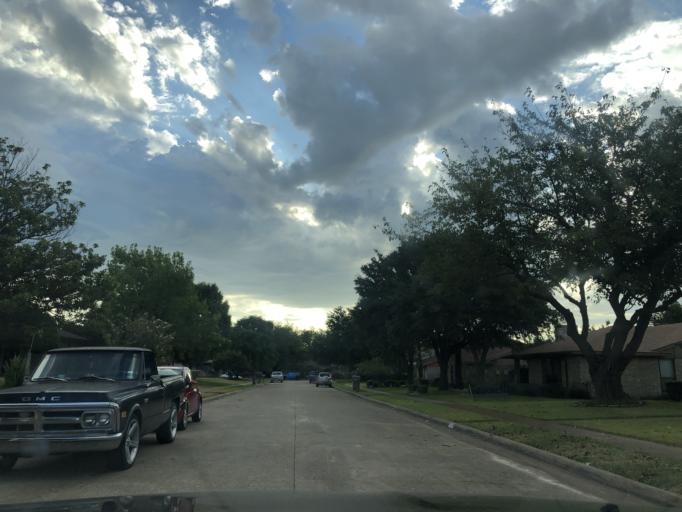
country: US
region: Texas
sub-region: Dallas County
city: Garland
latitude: 32.8736
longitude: -96.6555
